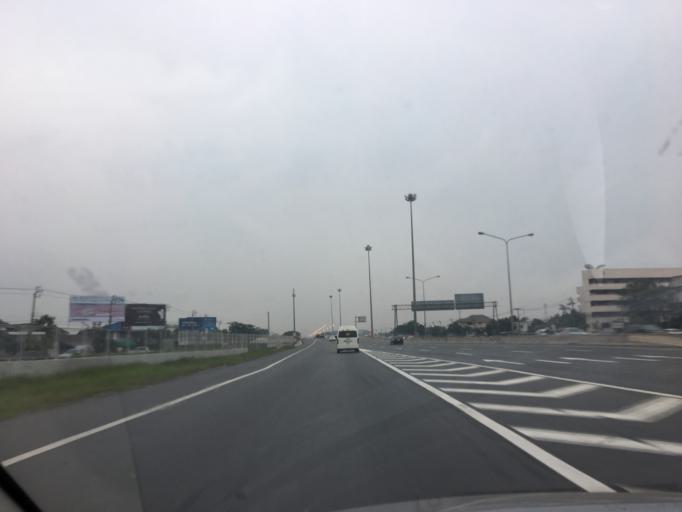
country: TH
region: Bangkok
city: Suan Luang
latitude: 13.7162
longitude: 100.7005
